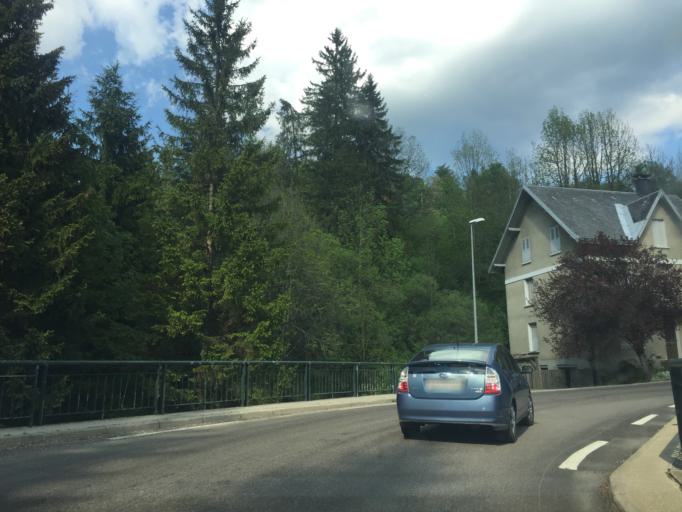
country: FR
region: Rhone-Alpes
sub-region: Departement de l'Isere
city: Saint-Hilaire
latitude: 45.3405
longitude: 5.8091
